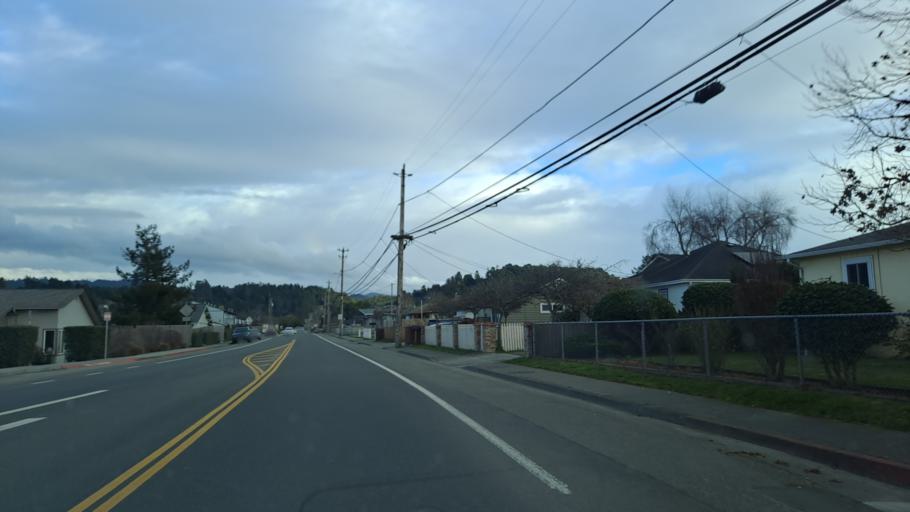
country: US
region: California
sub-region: Humboldt County
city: Fortuna
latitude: 40.5702
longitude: -124.1387
